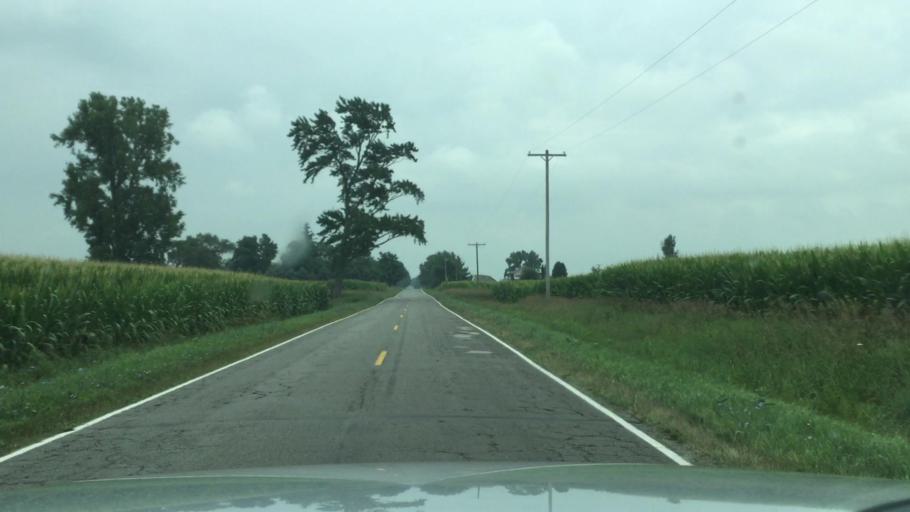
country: US
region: Michigan
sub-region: Shiawassee County
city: New Haven
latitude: 43.0847
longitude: -84.2262
